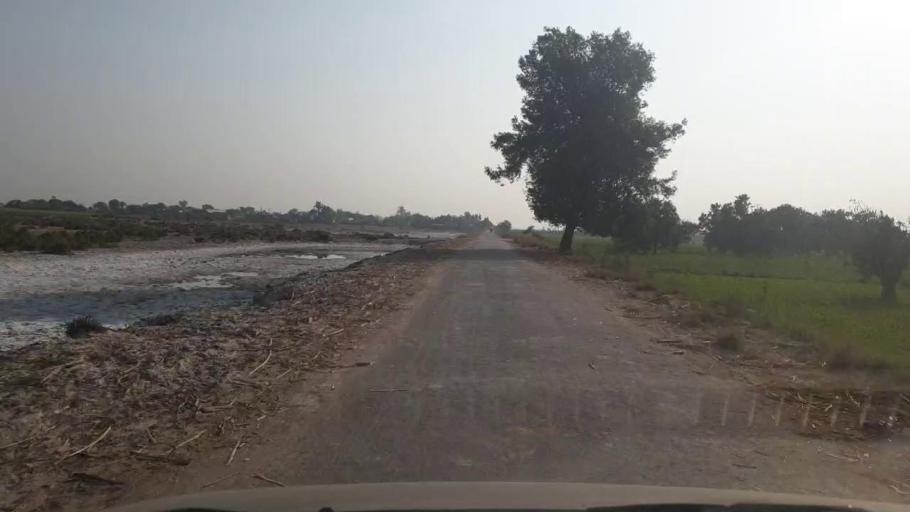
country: PK
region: Sindh
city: Digri
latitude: 25.2562
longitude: 69.1613
